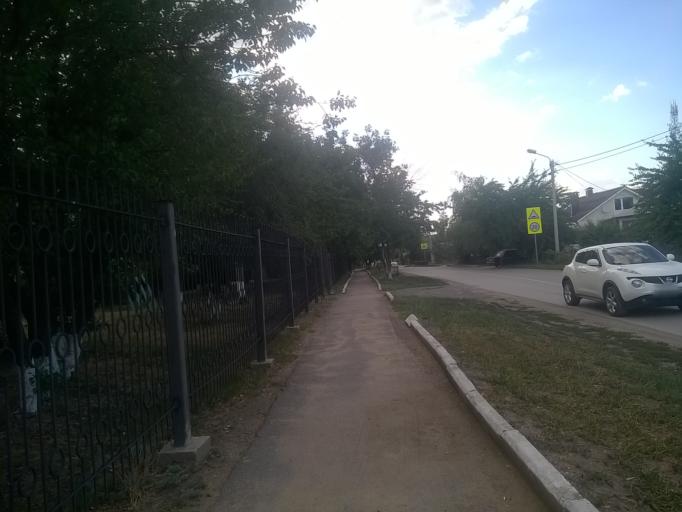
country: RU
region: Rostov
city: Donetsk
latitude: 48.3334
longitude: 39.9520
